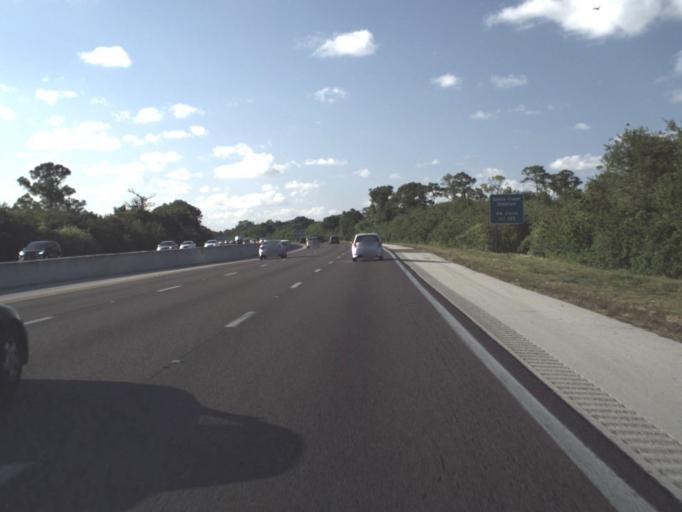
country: US
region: Florida
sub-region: Brevard County
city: Rockledge
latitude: 28.2813
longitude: -80.7331
